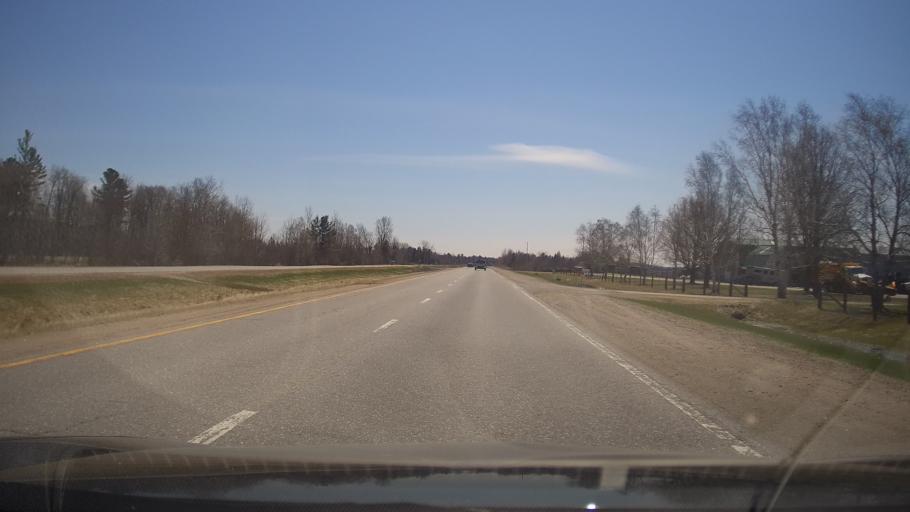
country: CA
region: Quebec
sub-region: Outaouais
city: Wakefield
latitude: 45.5217
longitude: -75.9903
